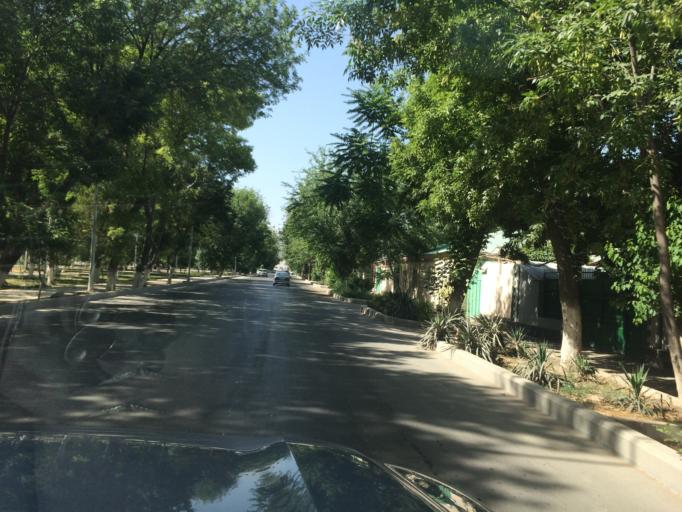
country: TM
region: Ahal
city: Ashgabat
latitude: 37.9489
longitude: 58.3614
